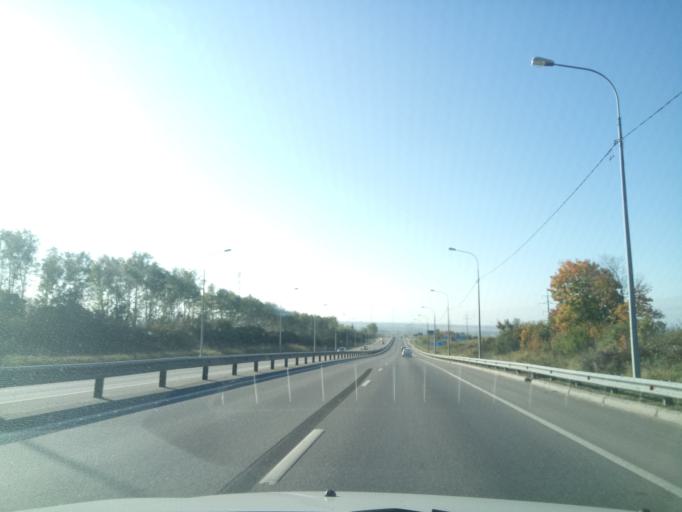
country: RU
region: Nizjnij Novgorod
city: Burevestnik
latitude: 56.1995
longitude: 43.9251
